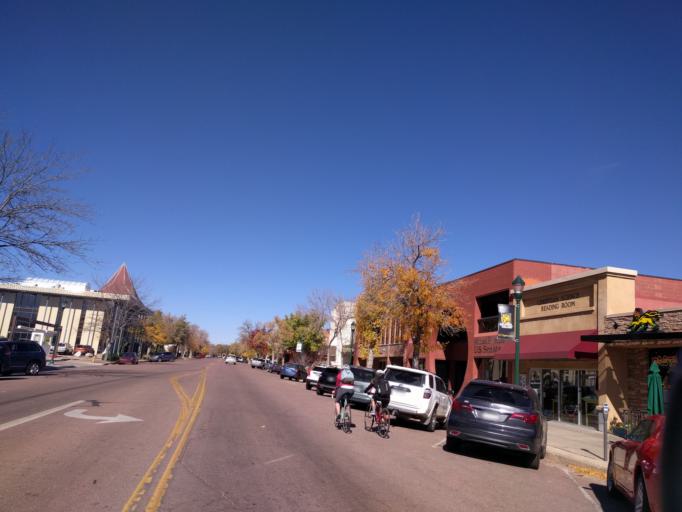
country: US
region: Colorado
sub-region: El Paso County
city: Colorado Springs
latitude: 38.8397
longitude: -104.8232
